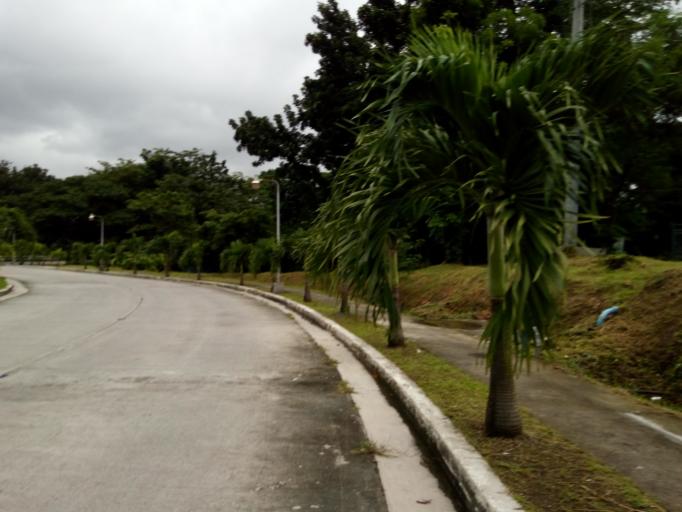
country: PH
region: Metro Manila
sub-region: Quezon City
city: Quezon City
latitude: 14.6502
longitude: 121.0707
